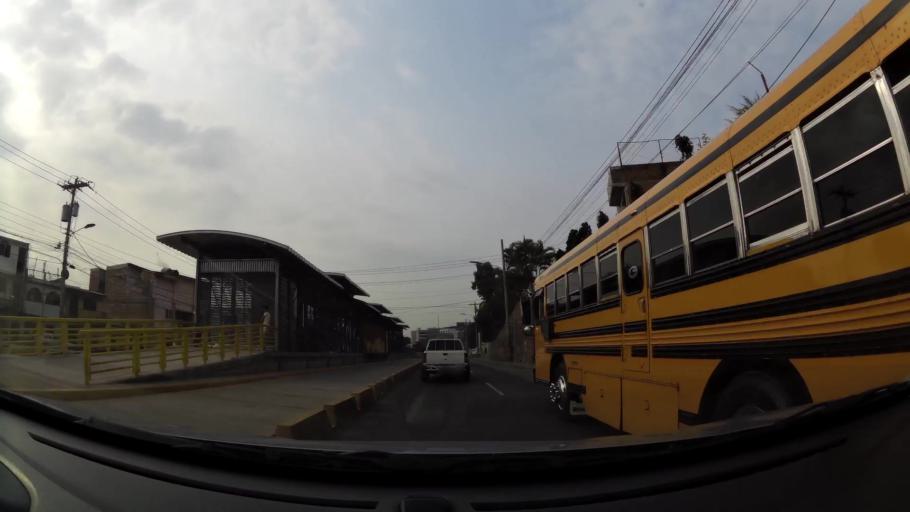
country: HN
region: Francisco Morazan
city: Tegucigalpa
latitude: 14.0935
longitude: -87.1981
